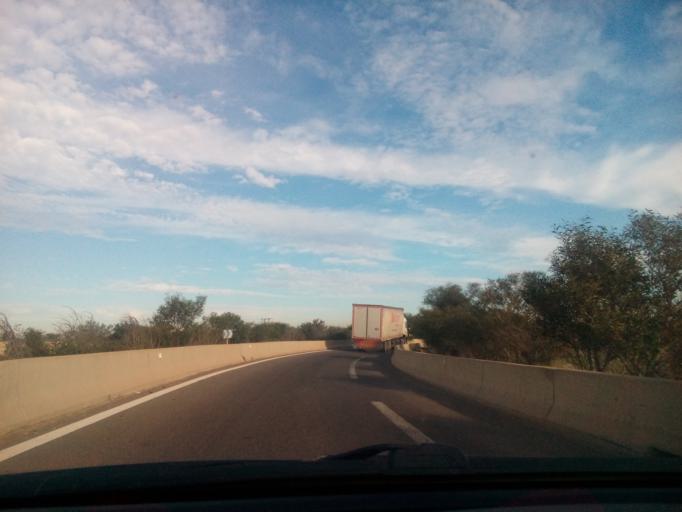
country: DZ
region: Mascara
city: Sig
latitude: 35.5840
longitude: -0.2202
